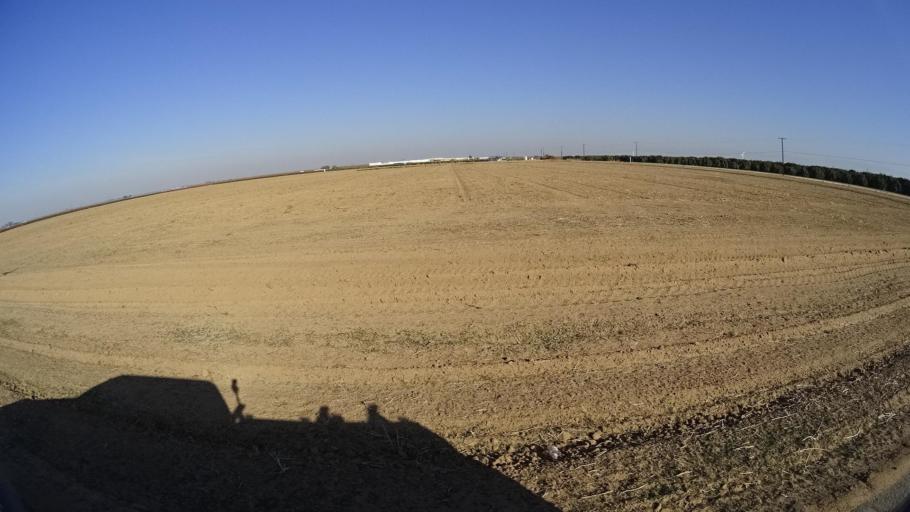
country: US
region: California
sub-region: Tulare County
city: Richgrove
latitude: 35.7325
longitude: -119.1439
